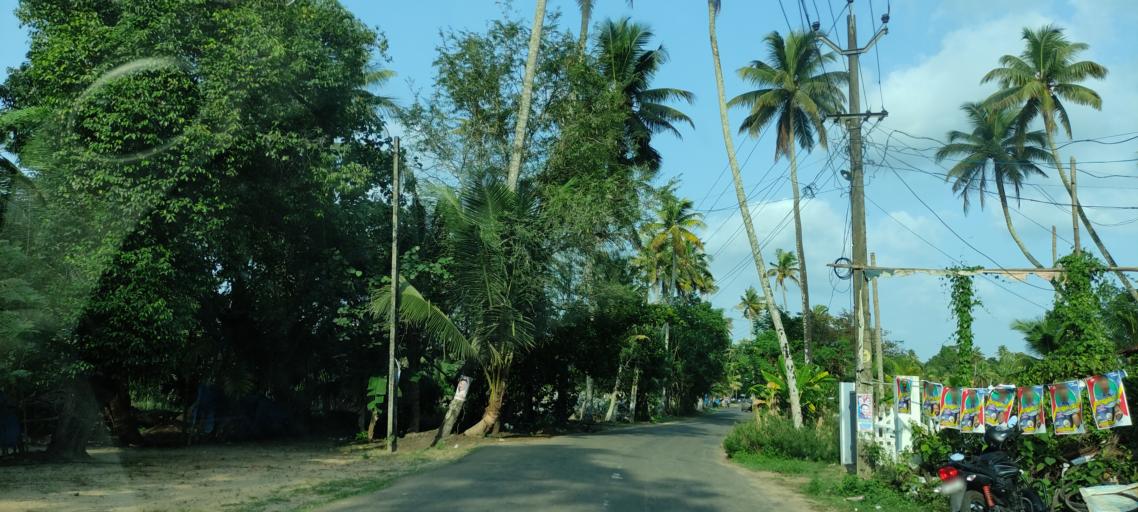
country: IN
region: Kerala
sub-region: Alappuzha
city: Vayalar
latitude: 9.7281
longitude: 76.2958
